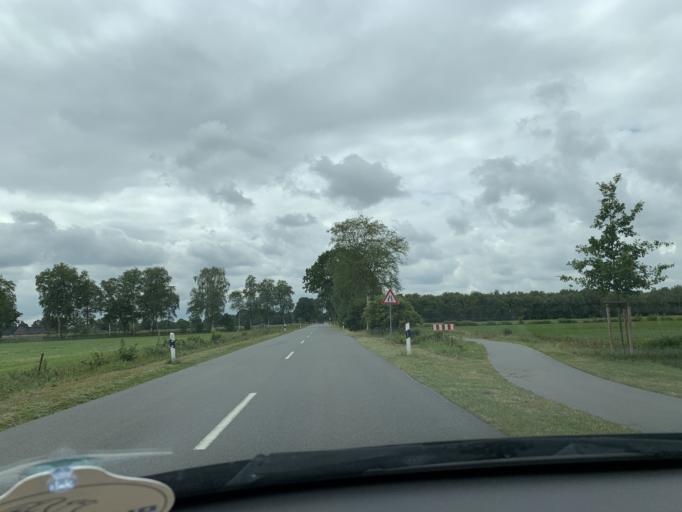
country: DE
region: Lower Saxony
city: Bockhorn
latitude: 53.3206
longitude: 8.0177
